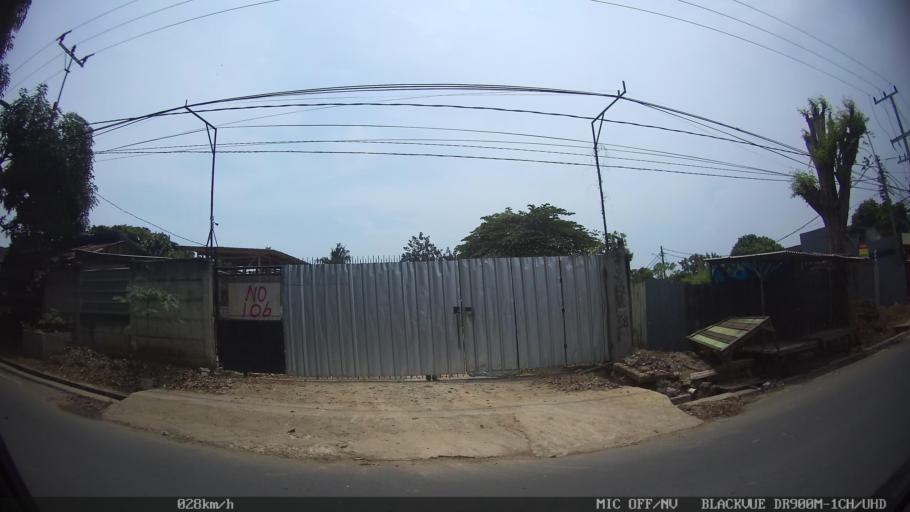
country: ID
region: Lampung
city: Bandarlampung
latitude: -5.4115
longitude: 105.2817
